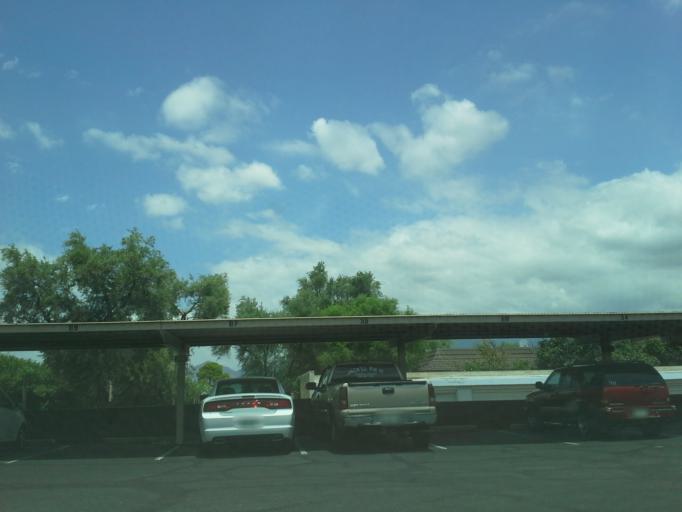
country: US
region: Arizona
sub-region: Pima County
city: Tucson
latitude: 32.2317
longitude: -110.9252
